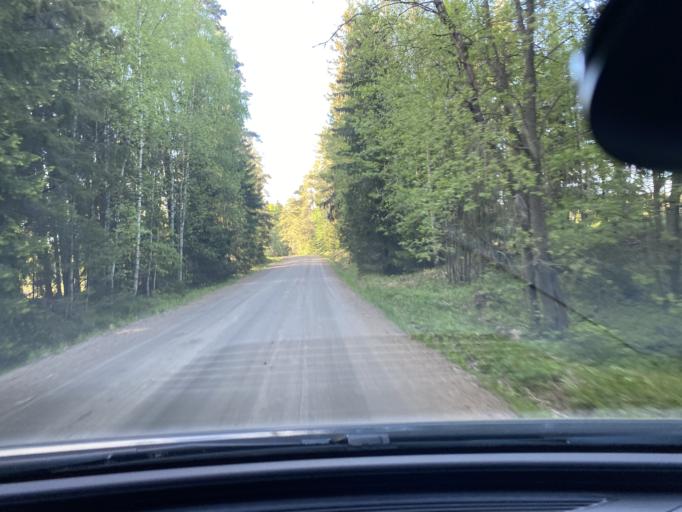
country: FI
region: Satakunta
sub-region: Pori
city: Huittinen
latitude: 61.1377
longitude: 22.8334
